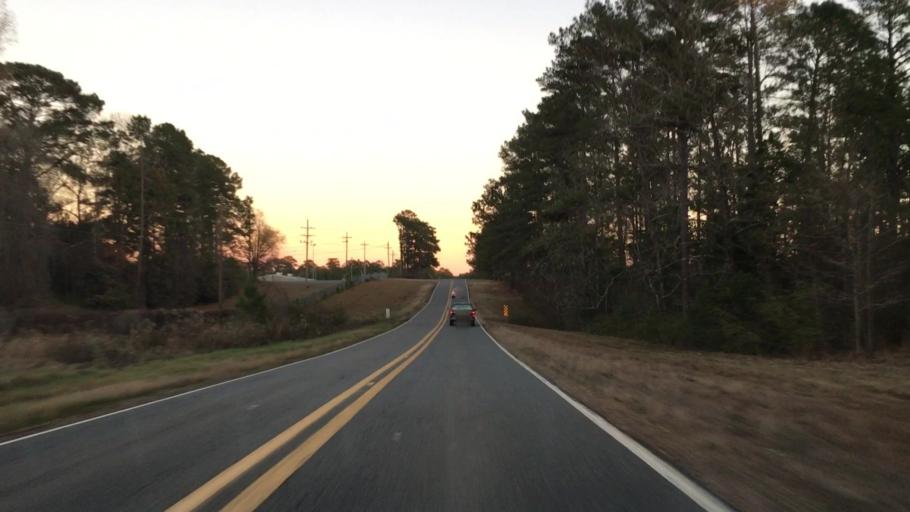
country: US
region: Louisiana
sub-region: Vernon Parish
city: Fort Polk South
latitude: 31.0290
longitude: -93.2063
